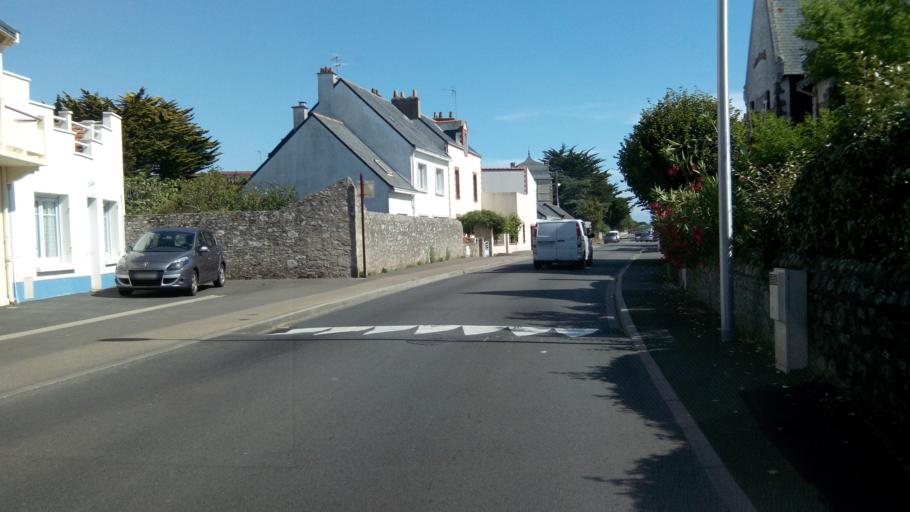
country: FR
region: Pays de la Loire
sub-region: Departement de la Loire-Atlantique
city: Le Croisic
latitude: 47.2888
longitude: -2.5108
